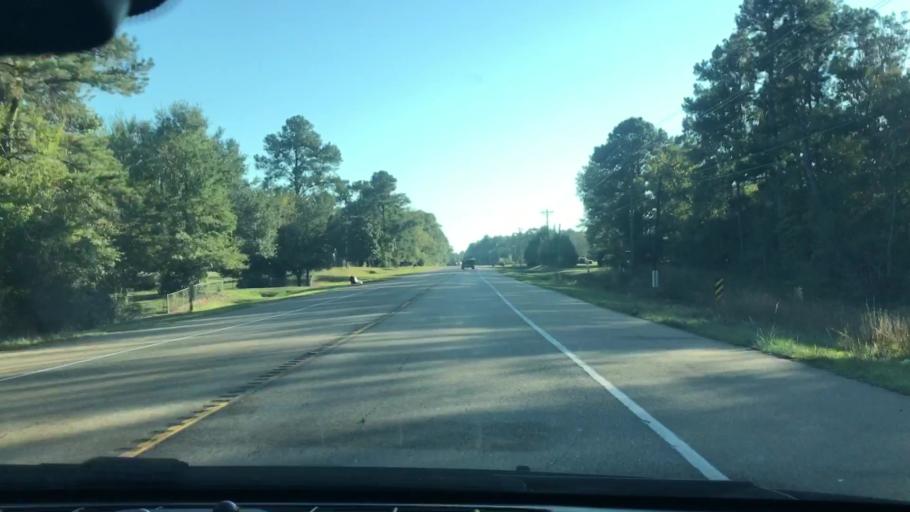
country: US
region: Louisiana
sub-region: Saint Tammany Parish
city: Abita Springs
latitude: 30.5498
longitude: -89.8740
